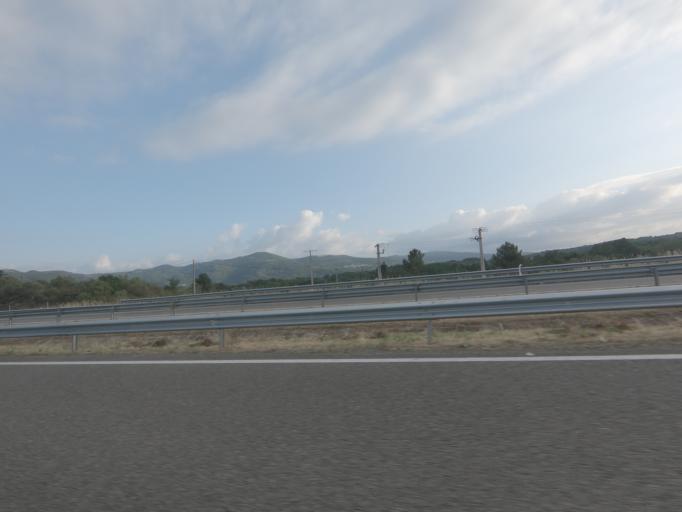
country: ES
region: Galicia
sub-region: Provincia de Ourense
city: Allariz
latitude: 42.2058
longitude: -7.8034
